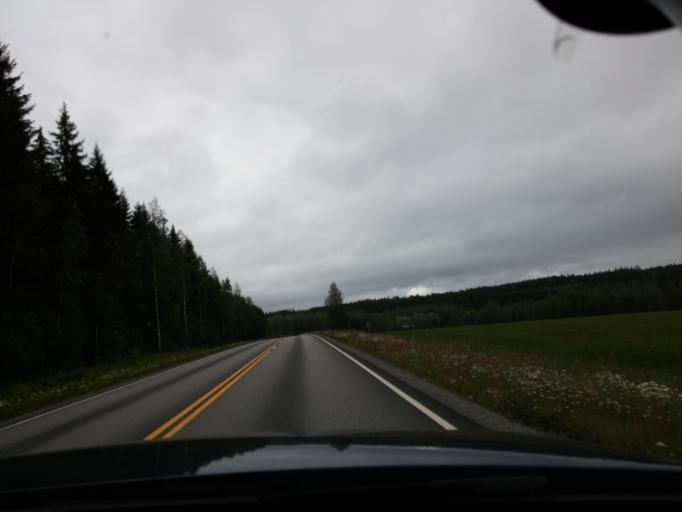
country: FI
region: Central Finland
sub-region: Saarijaervi-Viitasaari
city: Saarijaervi
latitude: 62.6850
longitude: 25.2508
